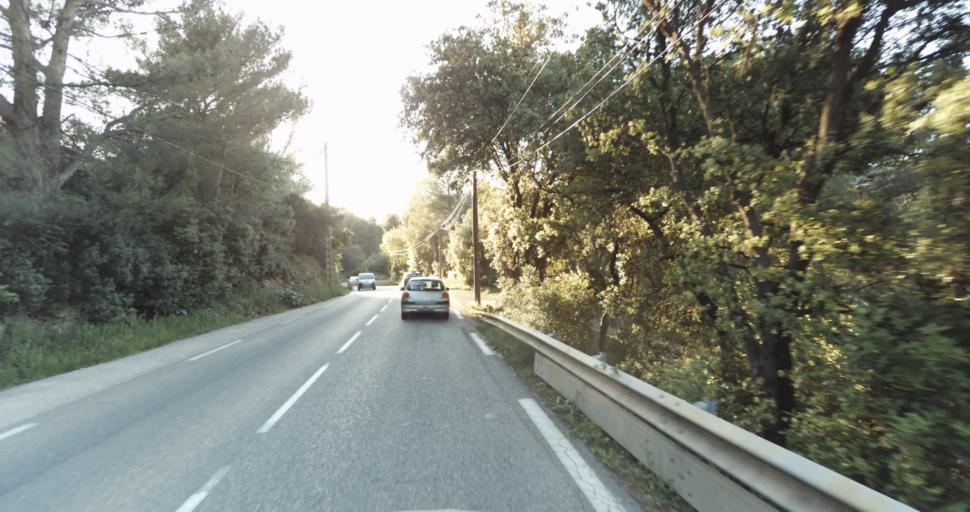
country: FR
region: Provence-Alpes-Cote d'Azur
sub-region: Departement du Var
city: La Valette-du-Var
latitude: 43.1575
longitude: 5.9581
